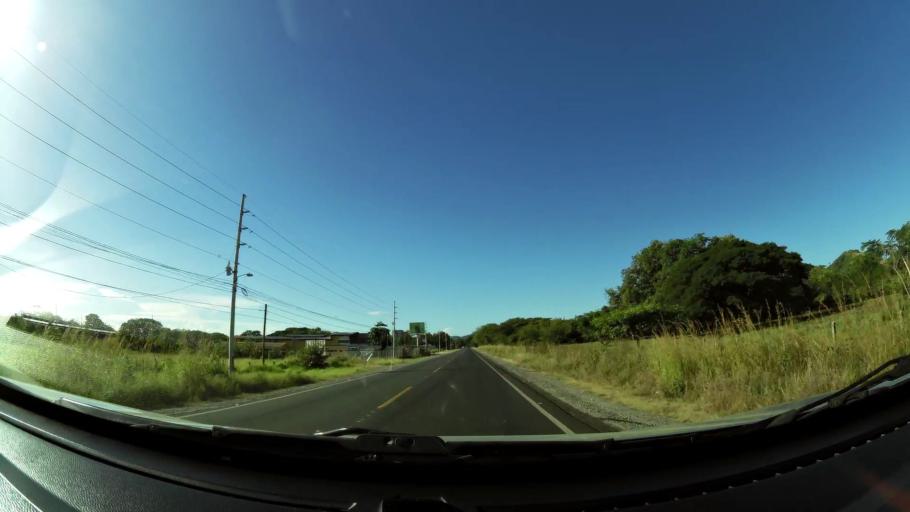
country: CR
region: Guanacaste
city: Belen
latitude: 10.4249
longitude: -85.5716
